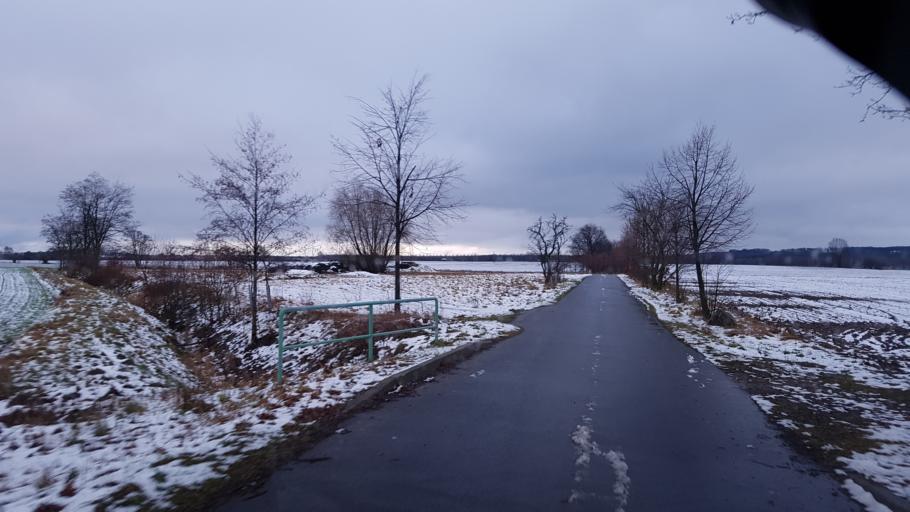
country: DE
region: Brandenburg
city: Crinitz
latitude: 51.7878
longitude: 13.7464
